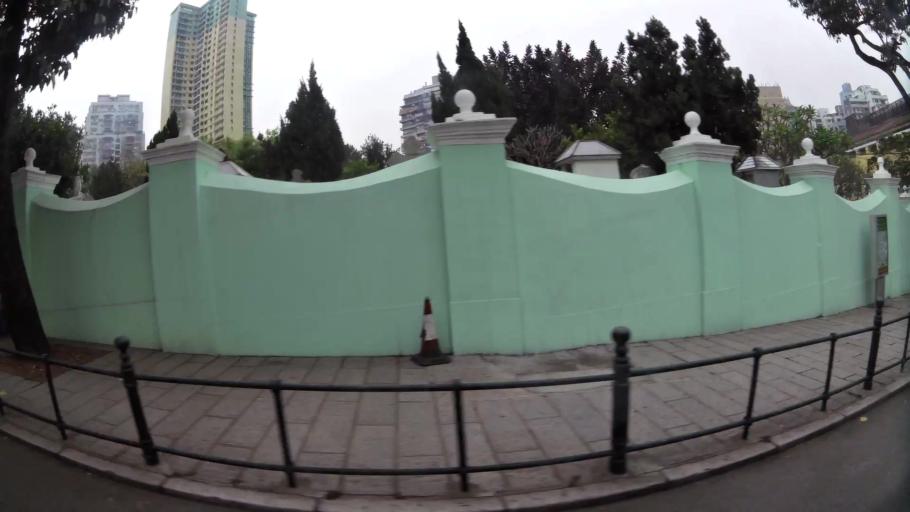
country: MO
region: Macau
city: Macau
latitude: 22.1982
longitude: 113.5461
